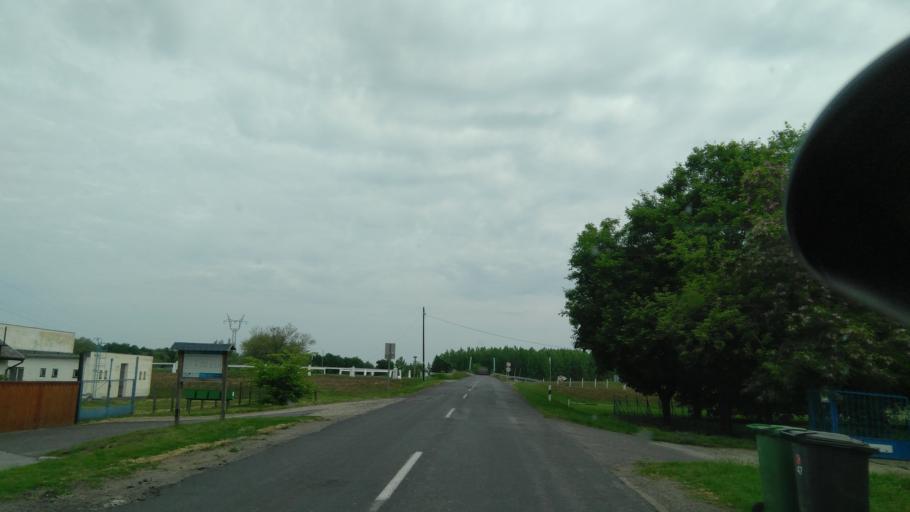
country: HU
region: Bekes
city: Szeghalom
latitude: 46.9861
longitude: 21.1831
